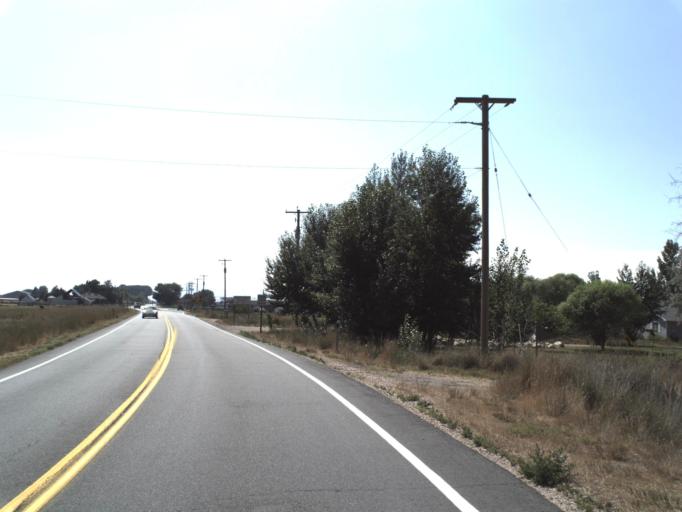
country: US
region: Utah
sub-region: Weber County
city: Plain City
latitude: 41.2448
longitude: -112.0846
